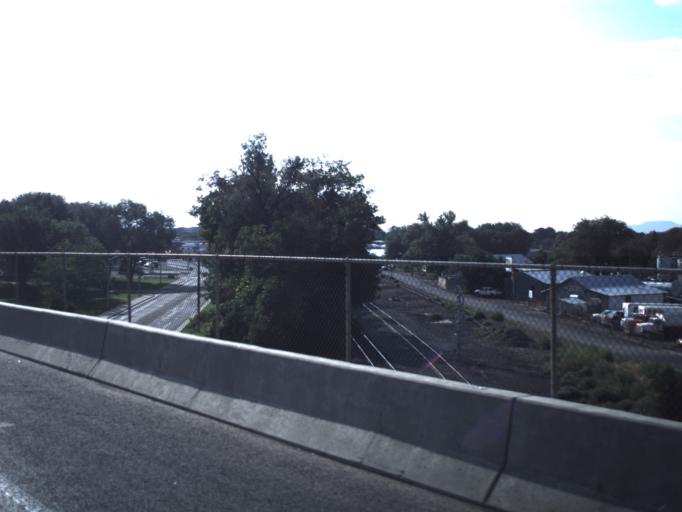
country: US
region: Utah
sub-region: Carbon County
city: Price
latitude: 39.6009
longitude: -110.8183
